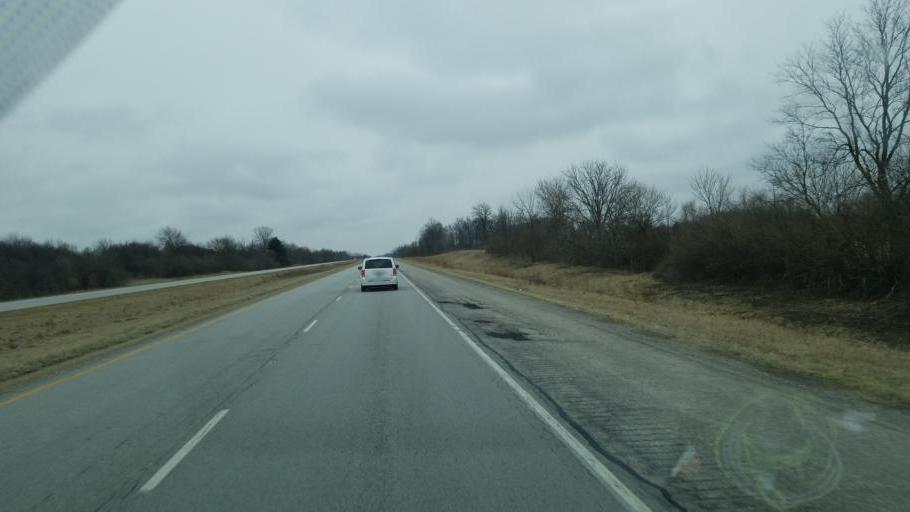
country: US
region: Indiana
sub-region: Fulton County
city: Rochester
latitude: 40.9767
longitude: -86.1683
